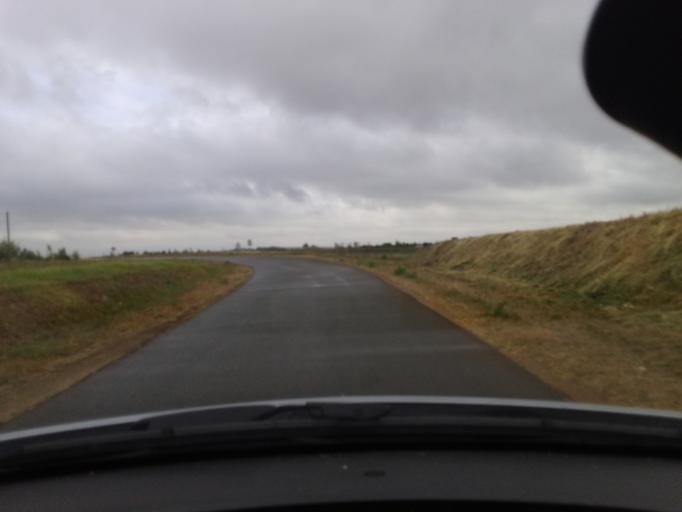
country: FR
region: Pays de la Loire
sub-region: Departement de la Vendee
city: Lucon
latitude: 46.4712
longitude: -1.1561
